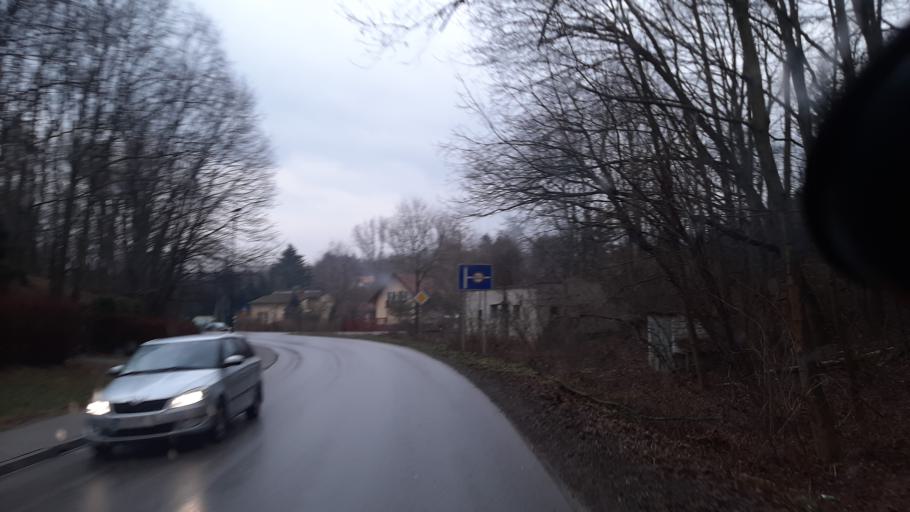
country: PL
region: Lublin Voivodeship
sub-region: Powiat lubelski
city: Lublin
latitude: 51.3151
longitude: 22.5611
